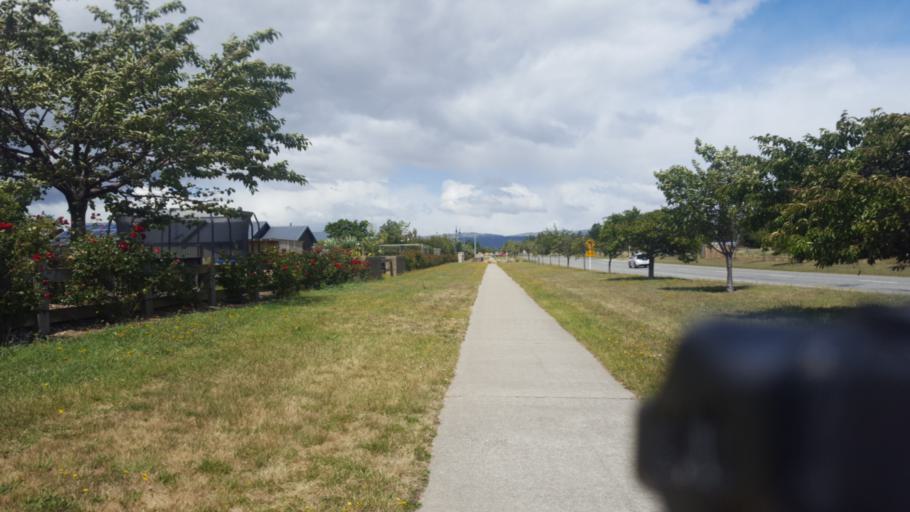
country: NZ
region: Otago
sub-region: Queenstown-Lakes District
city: Wanaka
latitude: -45.1966
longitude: 169.3296
